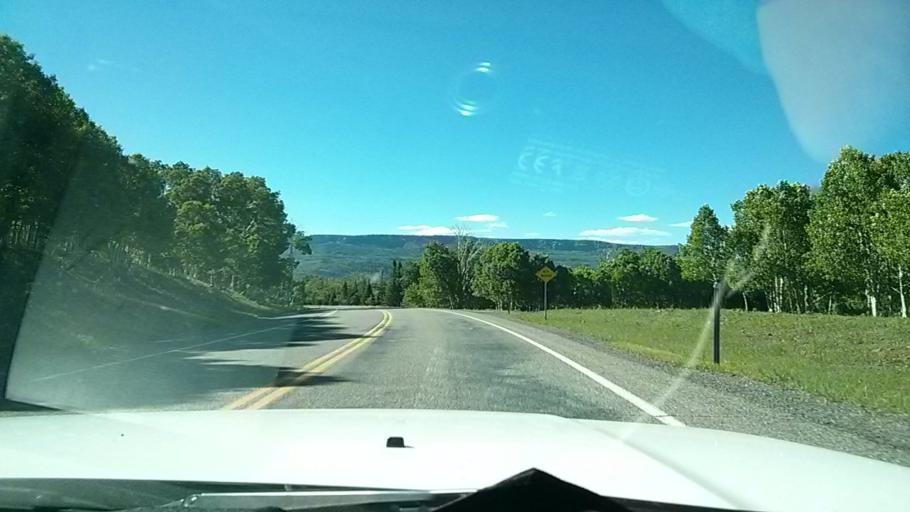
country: US
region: Utah
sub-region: Wayne County
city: Loa
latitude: 38.0671
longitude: -111.3295
